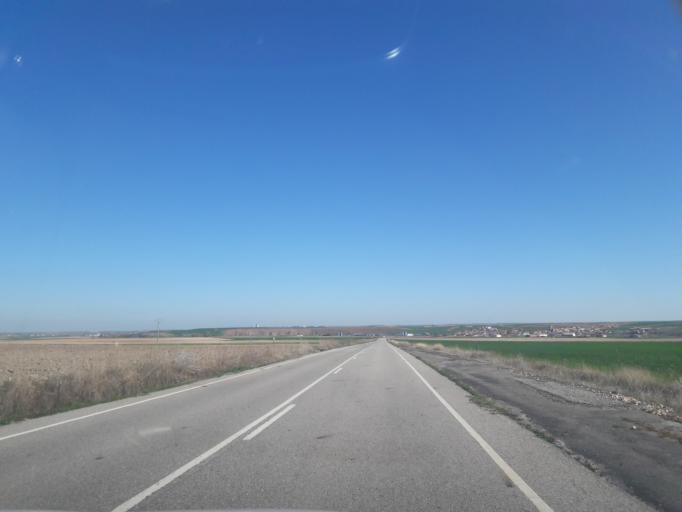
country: ES
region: Castille and Leon
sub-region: Provincia de Salamanca
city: Mancera de Abajo
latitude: 40.8248
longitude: -5.2087
